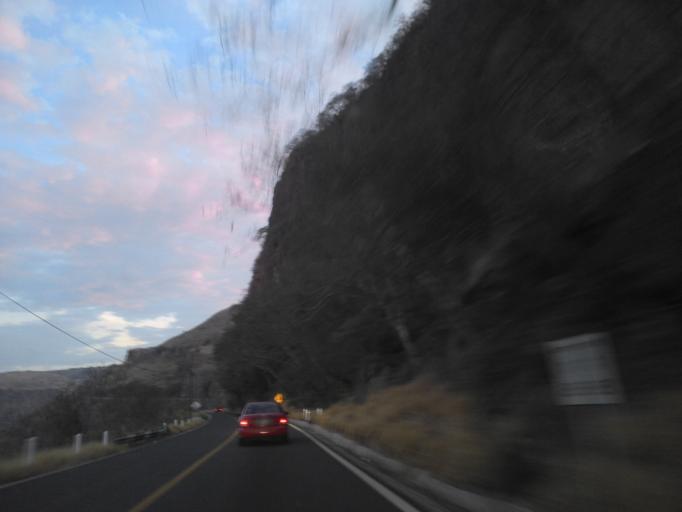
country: MX
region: Jalisco
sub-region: Zapopan
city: San Isidro
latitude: 20.8133
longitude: -103.3368
